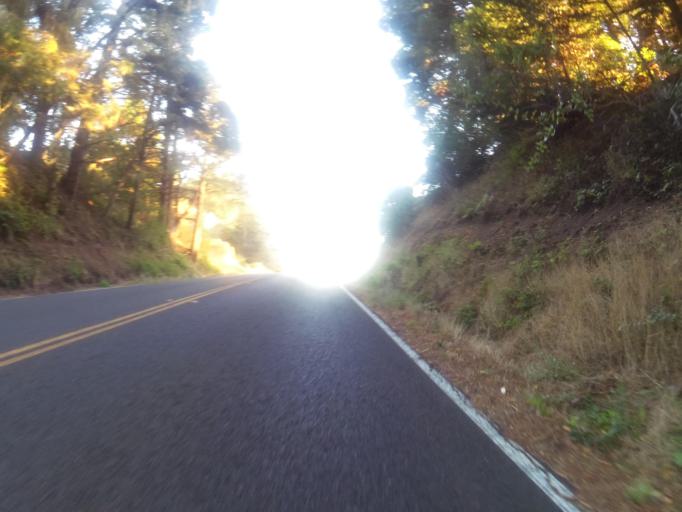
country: US
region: California
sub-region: Sonoma County
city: Sea Ranch
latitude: 38.6502
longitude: -123.3979
